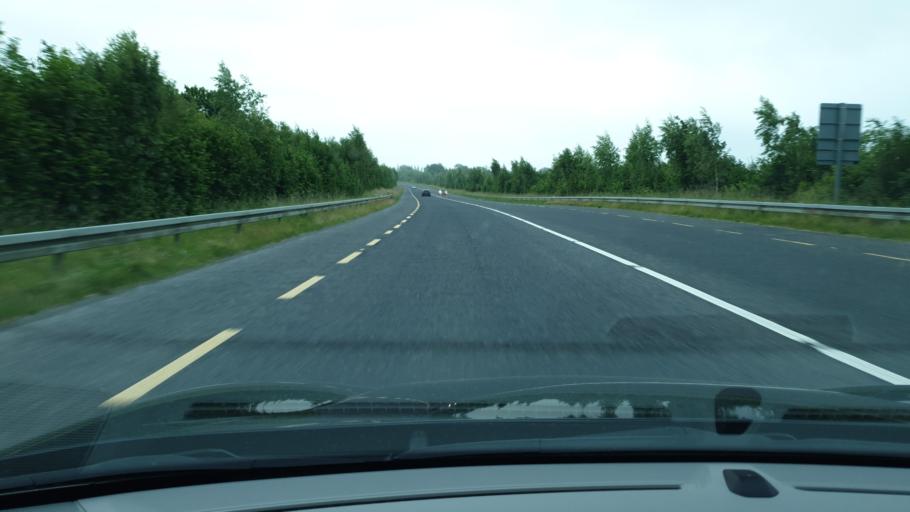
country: IE
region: Leinster
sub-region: An Mhi
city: Dunboyne
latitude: 53.4205
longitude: -6.4908
